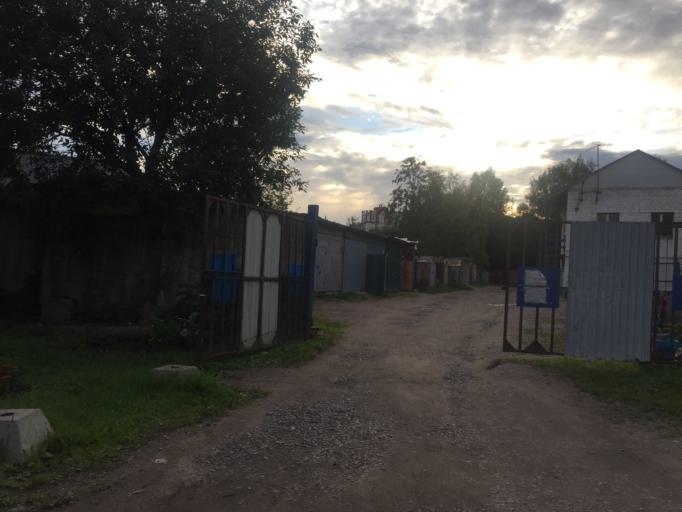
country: RU
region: Leningrad
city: Murino
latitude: 60.0417
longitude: 30.4716
